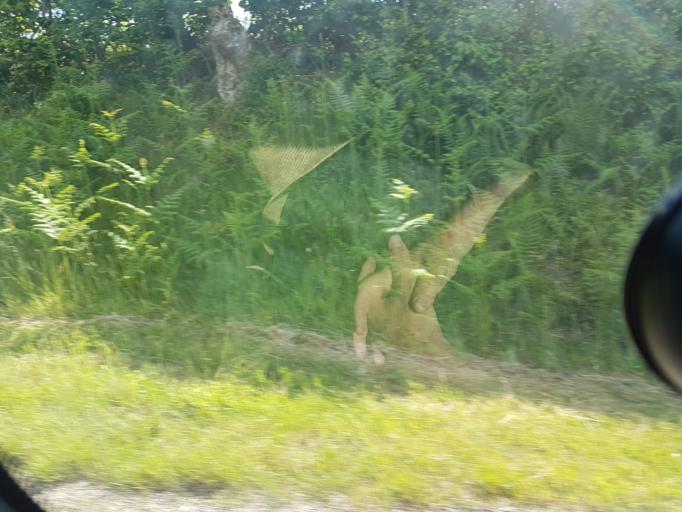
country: FR
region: Bourgogne
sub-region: Departement de la Cote-d'Or
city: Saulieu
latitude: 47.1653
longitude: 4.1811
